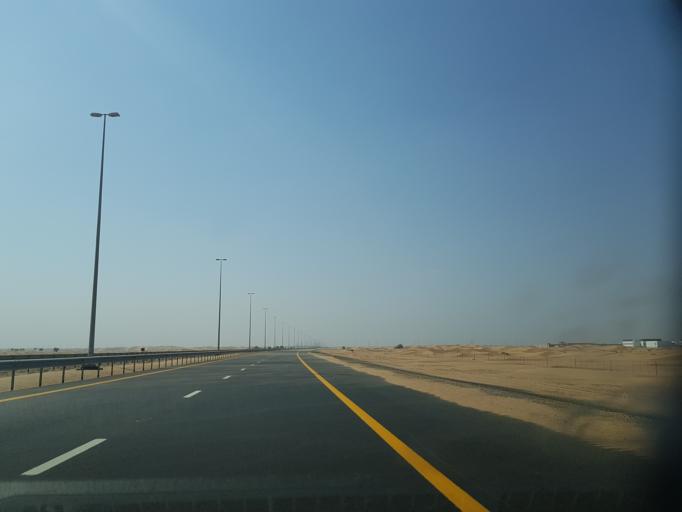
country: AE
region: Ash Shariqah
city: Sharjah
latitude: 25.2732
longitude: 55.6255
